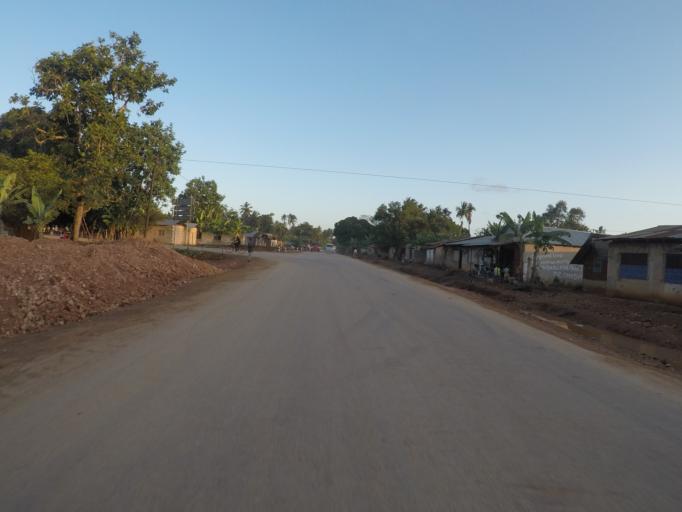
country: TZ
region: Zanzibar North
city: Gamba
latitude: -5.9563
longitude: 39.3063
